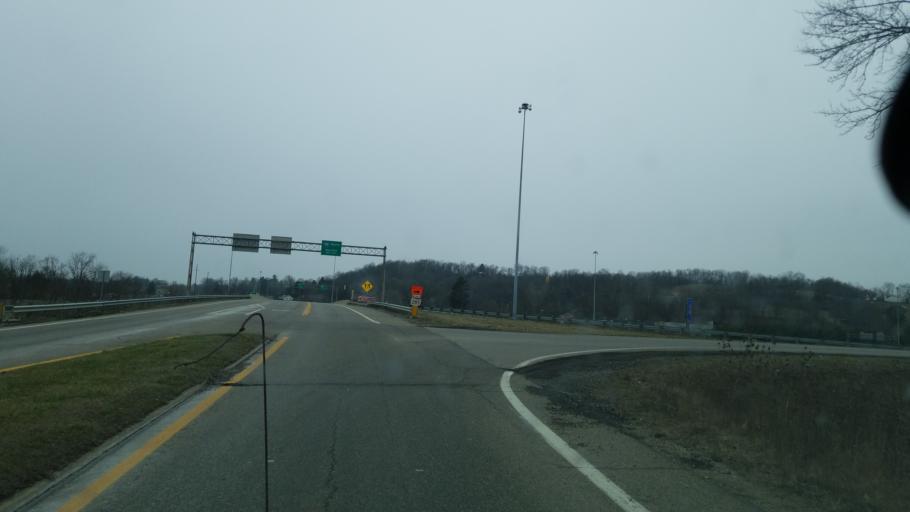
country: US
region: Ohio
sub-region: Guernsey County
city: Cambridge
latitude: 40.0275
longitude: -81.5589
